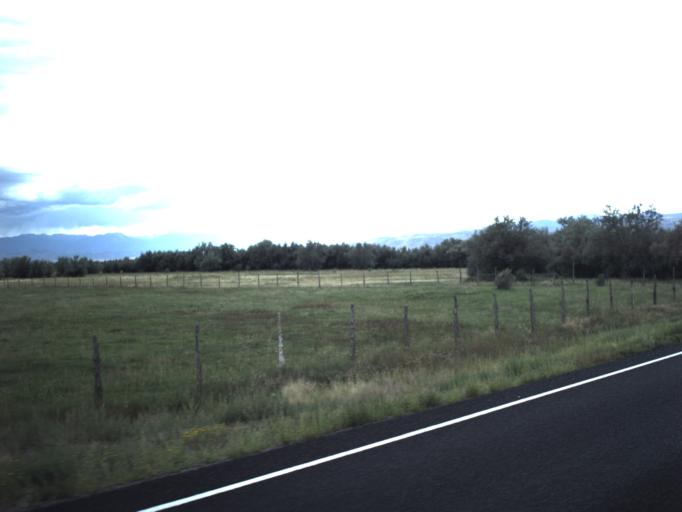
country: US
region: Utah
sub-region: Sevier County
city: Richfield
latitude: 38.7742
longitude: -112.0190
